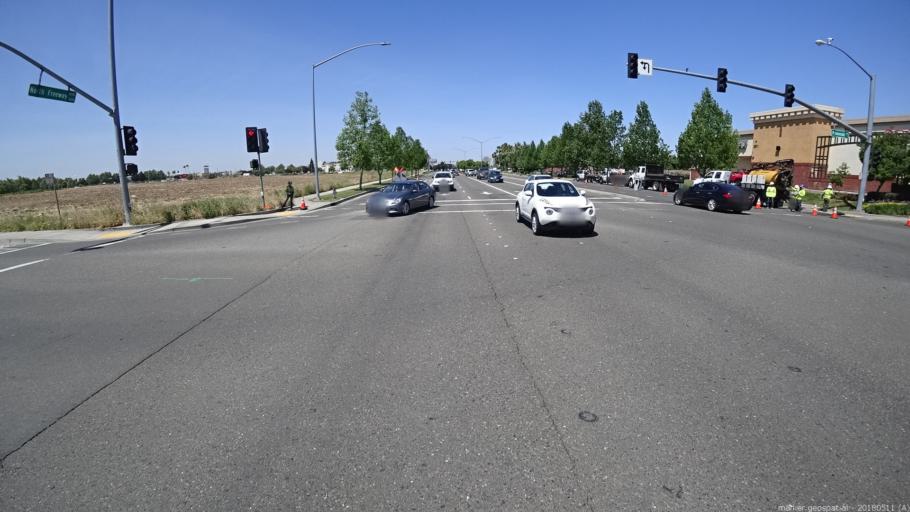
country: US
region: California
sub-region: Sacramento County
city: Sacramento
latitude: 38.6396
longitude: -121.4998
